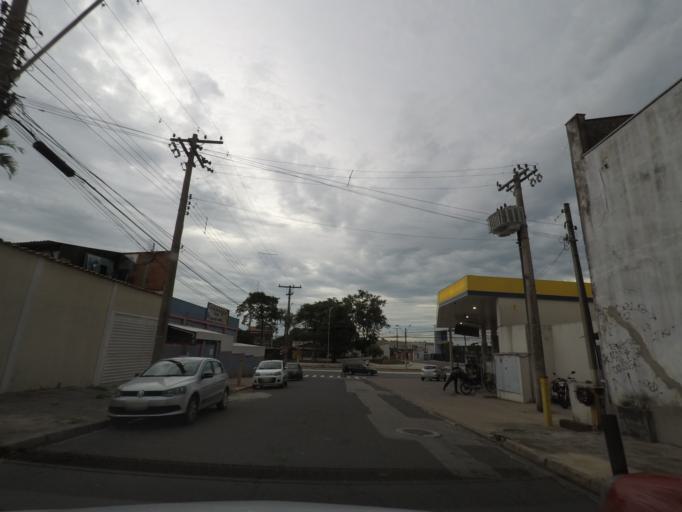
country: BR
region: Sao Paulo
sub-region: Campinas
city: Campinas
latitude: -22.9338
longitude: -47.0913
